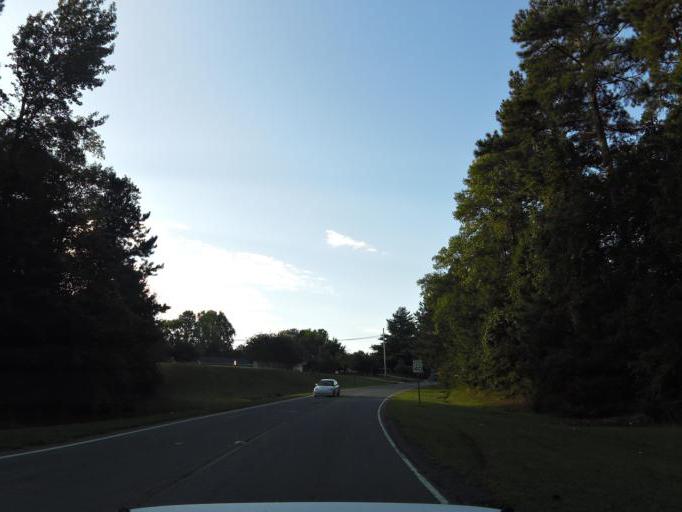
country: US
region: Georgia
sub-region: Cobb County
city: Kennesaw
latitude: 34.0196
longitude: -84.6248
